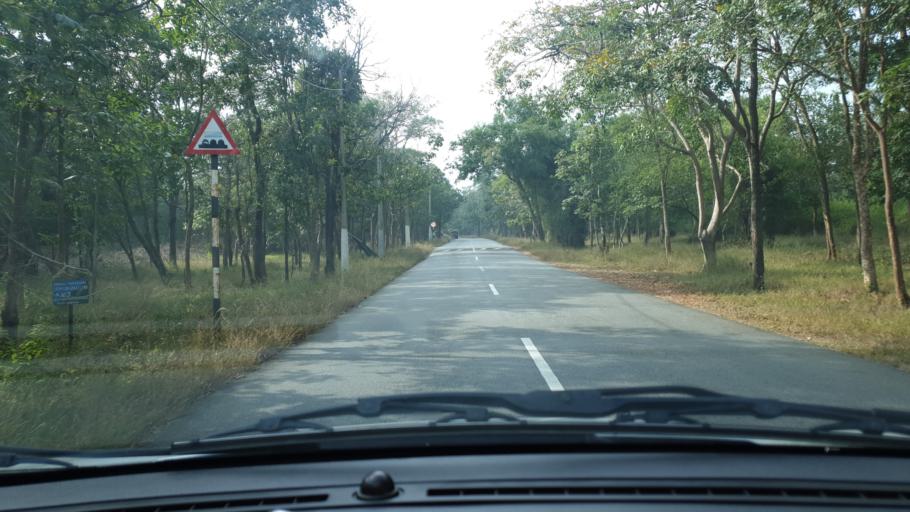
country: IN
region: Andhra Pradesh
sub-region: Kurnool
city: Srisailam
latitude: 16.2848
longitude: 78.7274
